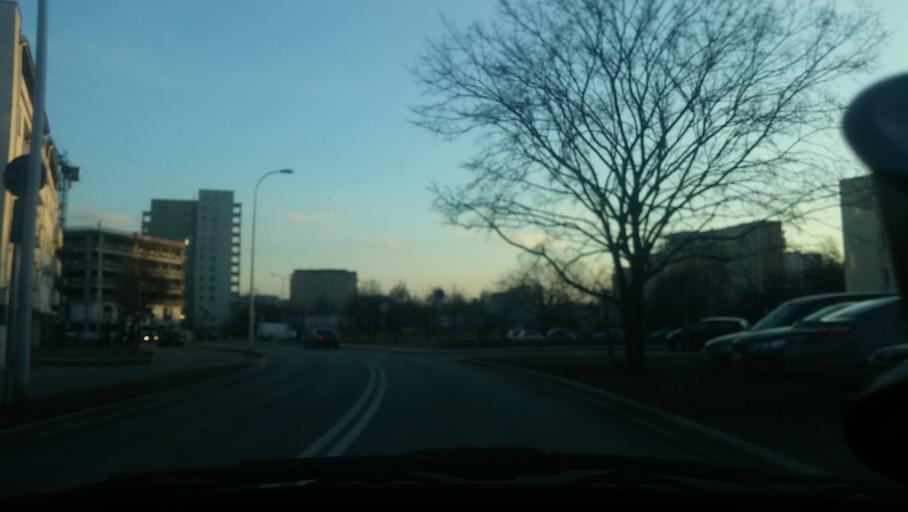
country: PL
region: Masovian Voivodeship
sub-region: Warszawa
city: Praga Poludnie
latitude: 52.2314
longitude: 21.0823
